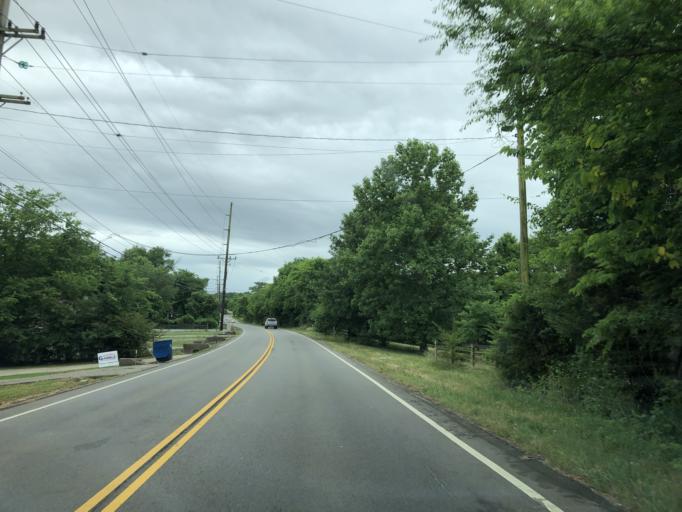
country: US
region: Tennessee
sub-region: Davidson County
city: Nashville
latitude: 36.2553
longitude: -86.7772
